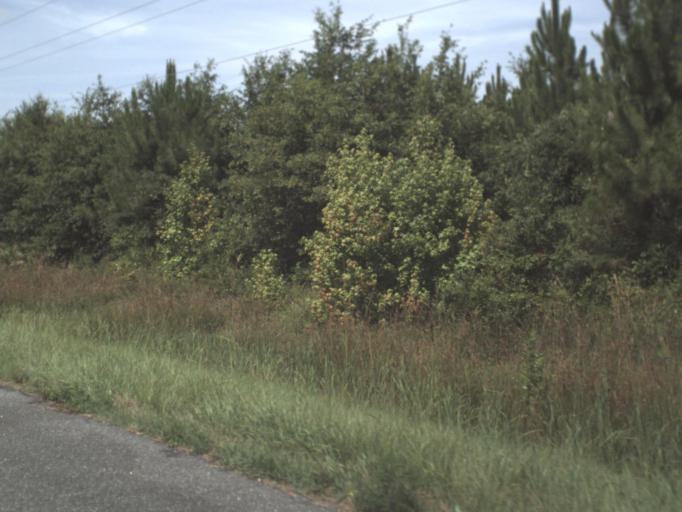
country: US
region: Florida
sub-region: Lafayette County
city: Mayo
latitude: 29.9844
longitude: -83.1997
